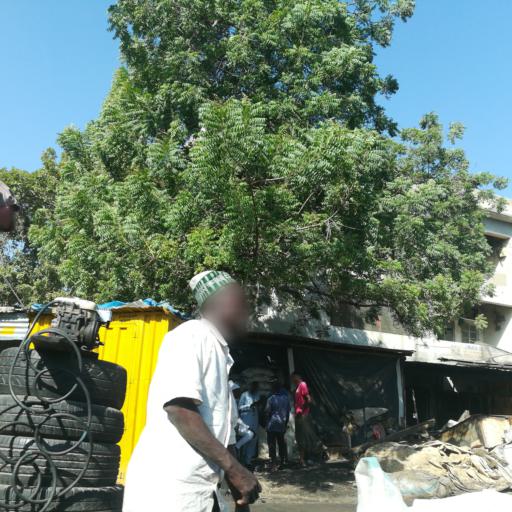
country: NG
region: Kano
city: Kano
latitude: 12.0109
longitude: 8.5326
